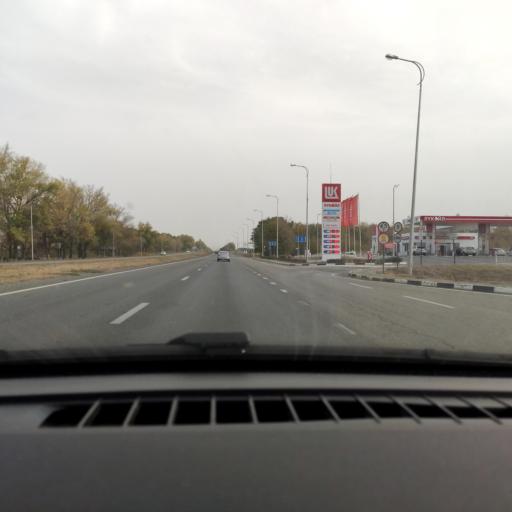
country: RU
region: Belgorod
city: Razumnoye
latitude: 50.6599
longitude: 36.6993
